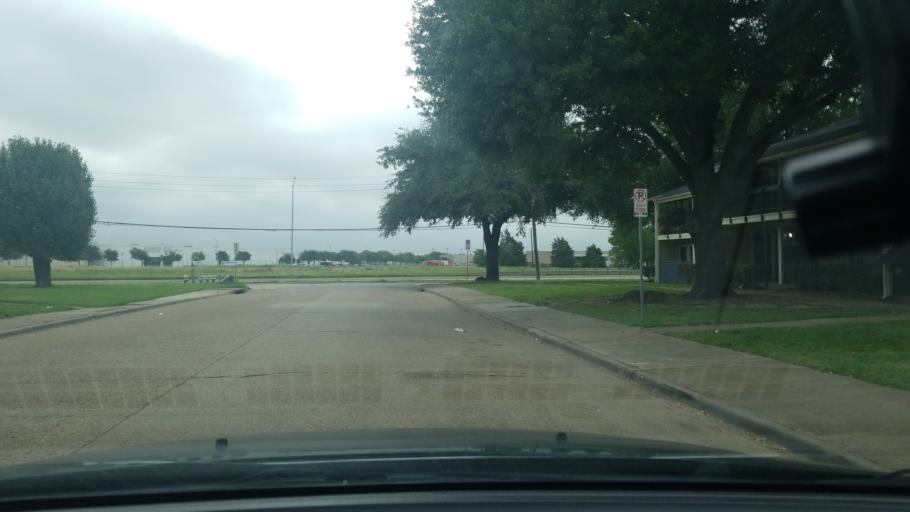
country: US
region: Texas
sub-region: Dallas County
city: Balch Springs
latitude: 32.7834
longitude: -96.6843
